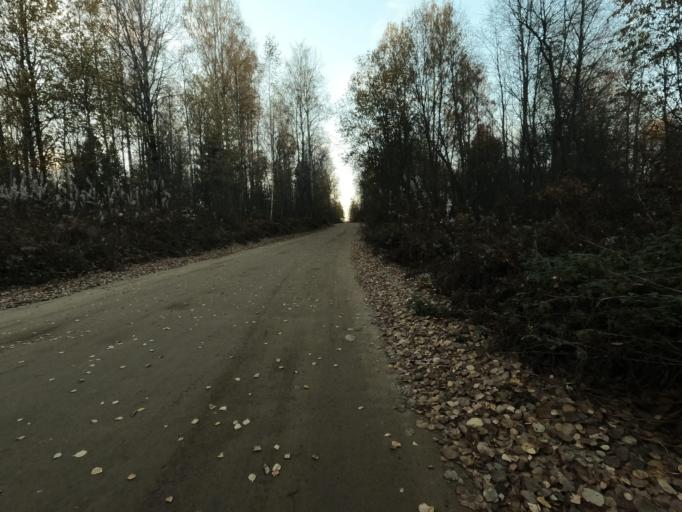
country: RU
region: Leningrad
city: Mga
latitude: 59.7544
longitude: 31.2826
